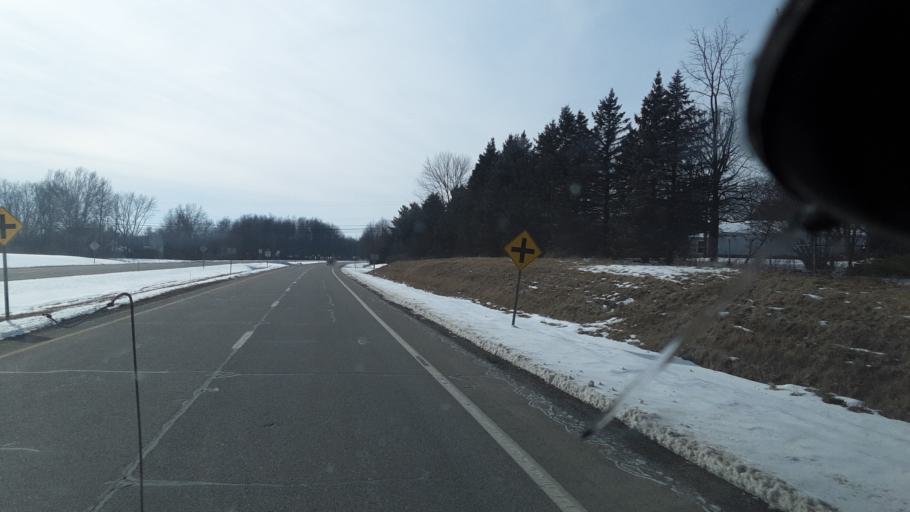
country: US
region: Ohio
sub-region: Portage County
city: Ravenna
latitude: 41.0311
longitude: -81.2141
